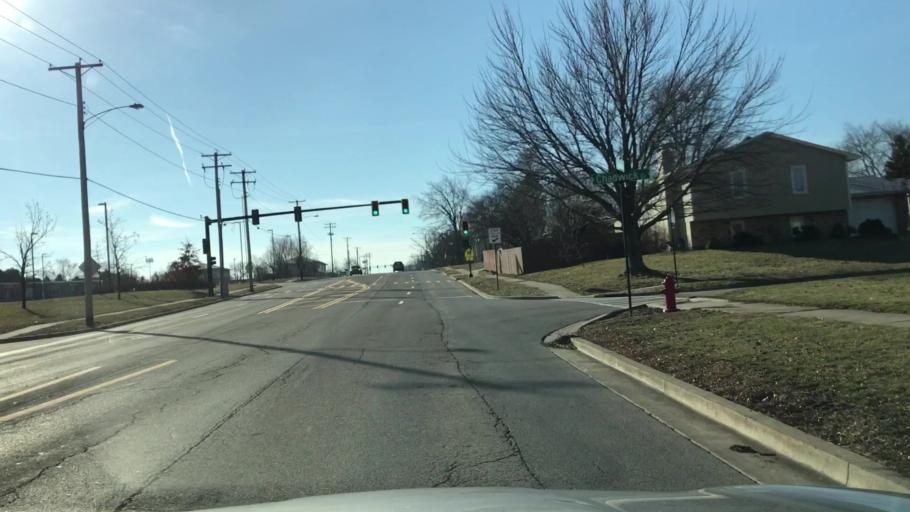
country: US
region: Illinois
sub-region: McLean County
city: Normal
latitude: 40.5140
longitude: -88.9608
